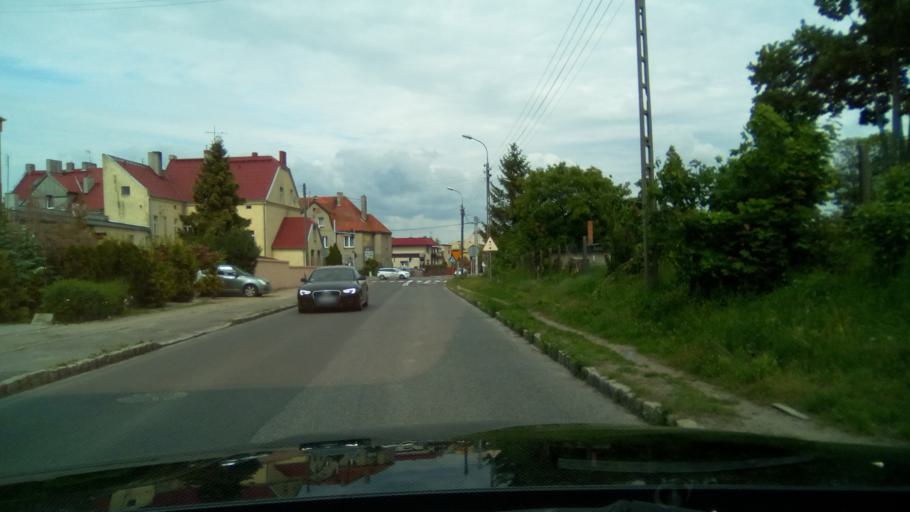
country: PL
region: Greater Poland Voivodeship
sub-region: Powiat gnieznienski
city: Gniezno
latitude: 52.5197
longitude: 17.6046
